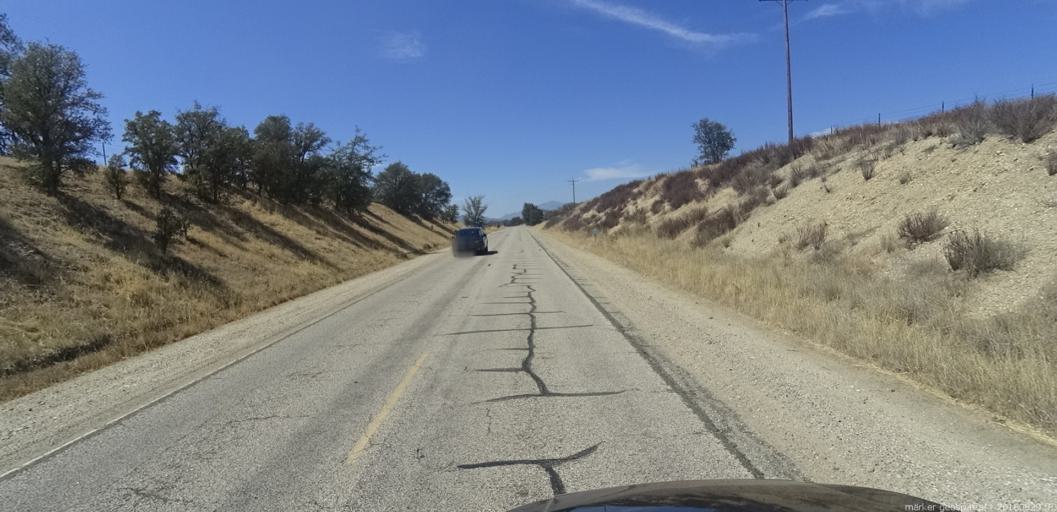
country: US
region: California
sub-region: Monterey County
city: King City
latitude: 35.9568
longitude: -121.1552
